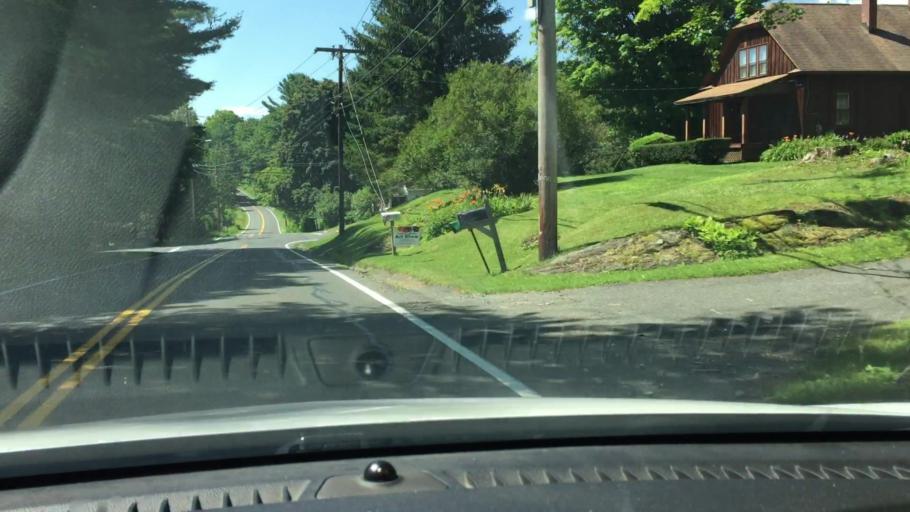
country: US
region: Massachusetts
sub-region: Berkshire County
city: Lenox
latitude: 42.3967
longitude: -73.2550
